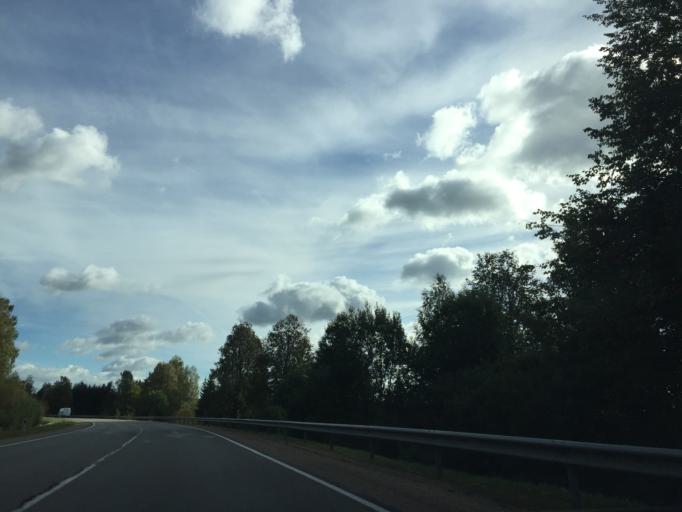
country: LV
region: Plavinu
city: Plavinas
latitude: 56.5875
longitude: 25.6015
